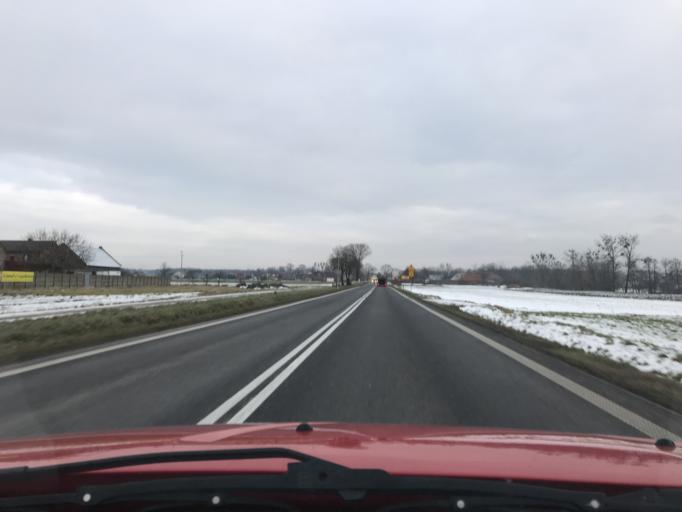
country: PL
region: Greater Poland Voivodeship
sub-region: Powiat pleszewski
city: Pleszew
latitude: 51.8876
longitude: 17.8509
